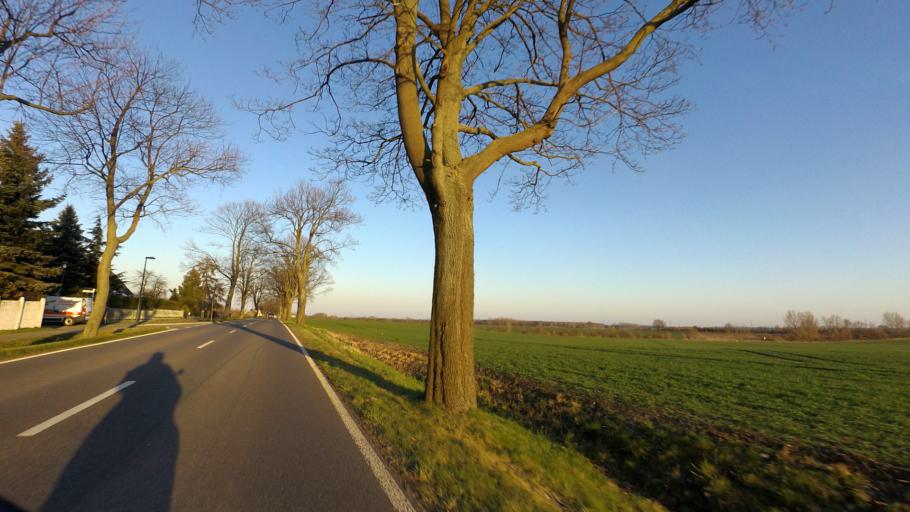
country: DE
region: Brandenburg
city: Ahrensfelde
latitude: 52.5725
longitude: 13.5994
